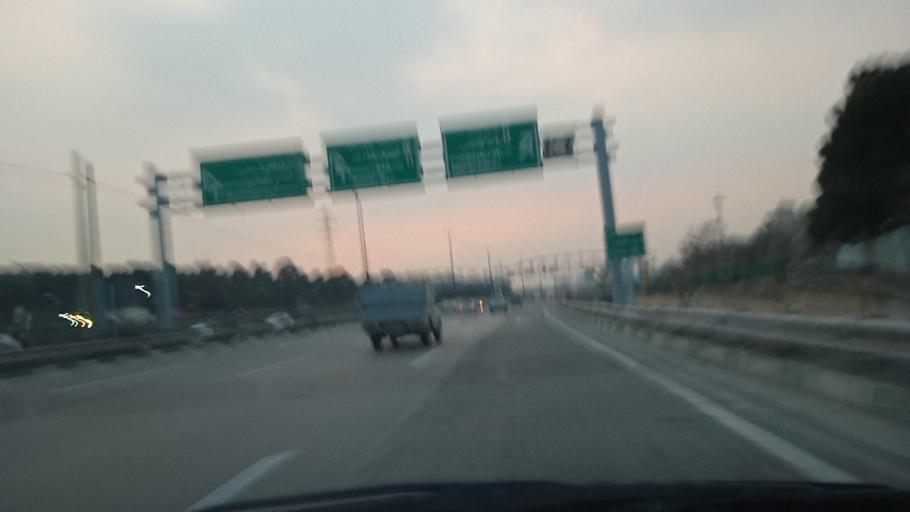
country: IR
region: Tehran
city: Tehran
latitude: 35.7220
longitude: 51.5293
